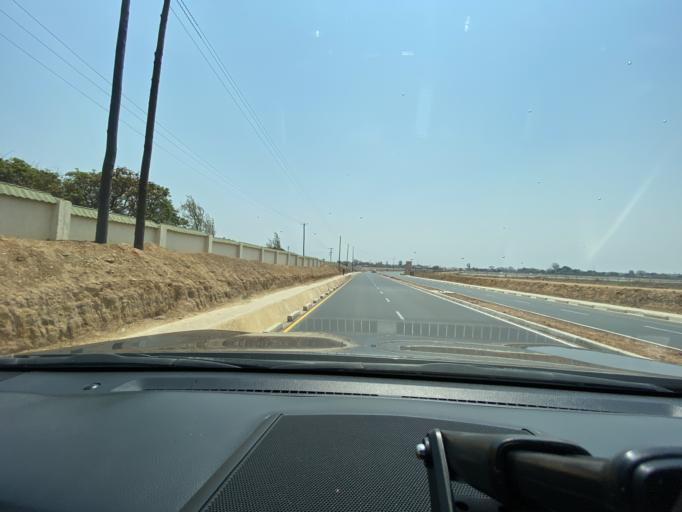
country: ZM
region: Lusaka
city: Lusaka
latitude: -15.3616
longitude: 28.3485
